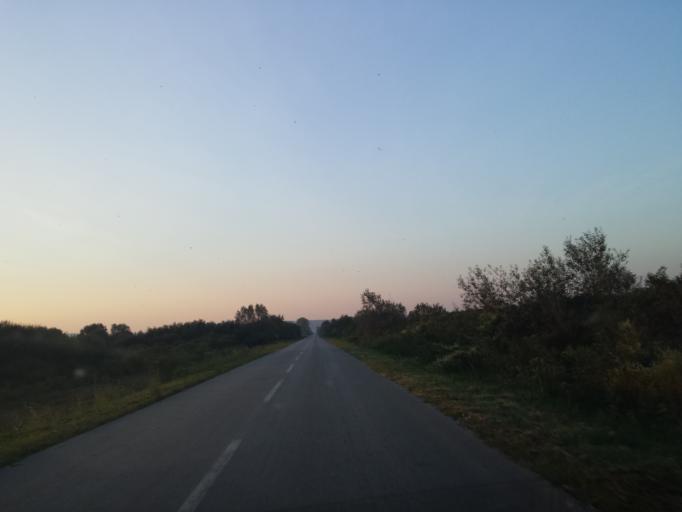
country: HR
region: Brodsko-Posavska
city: Oriovac
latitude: 45.1259
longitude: 17.8237
